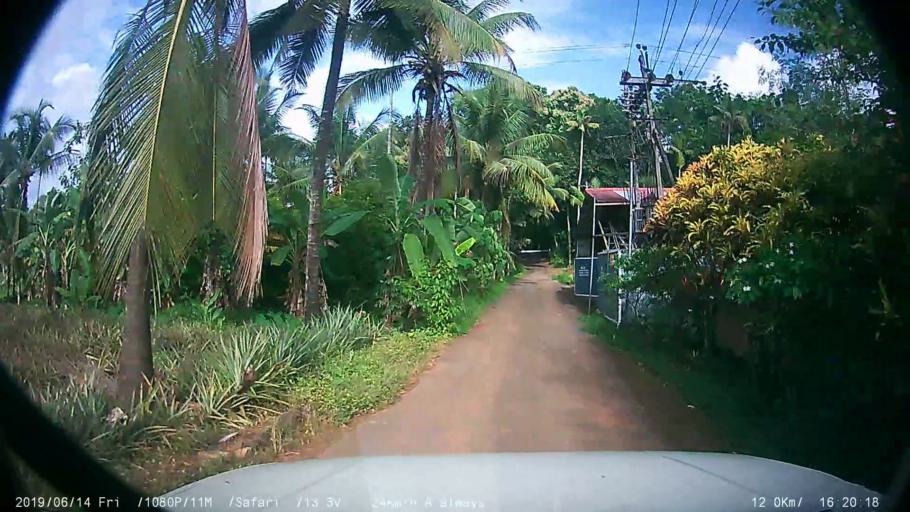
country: IN
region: Kerala
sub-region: Kottayam
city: Palackattumala
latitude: 9.7769
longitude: 76.6108
